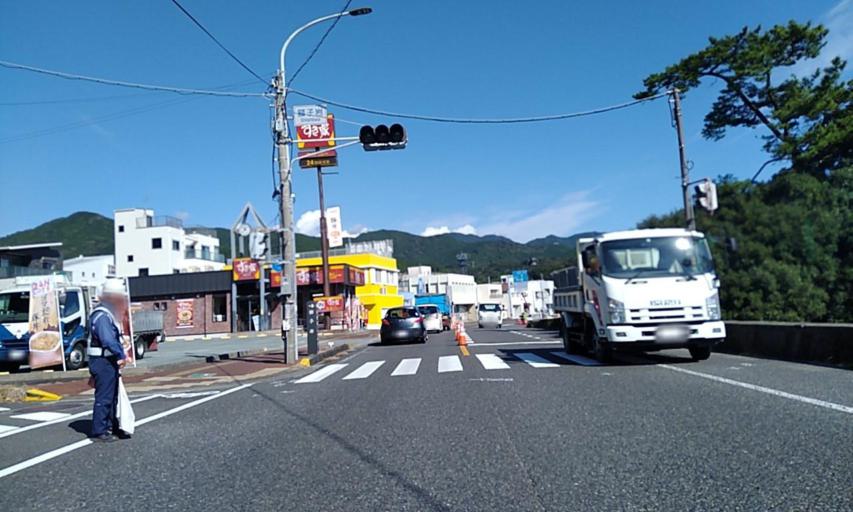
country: JP
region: Wakayama
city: Shingu
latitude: 33.8841
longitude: 136.0976
